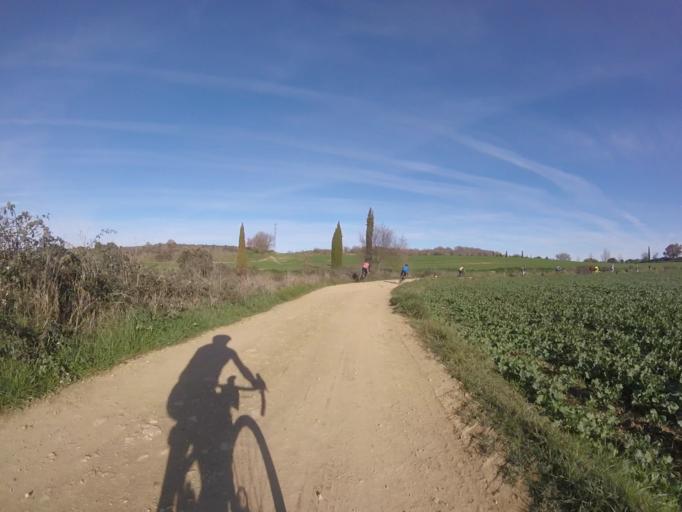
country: ES
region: Navarre
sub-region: Provincia de Navarra
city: Villatuerta
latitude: 42.6648
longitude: -1.9619
